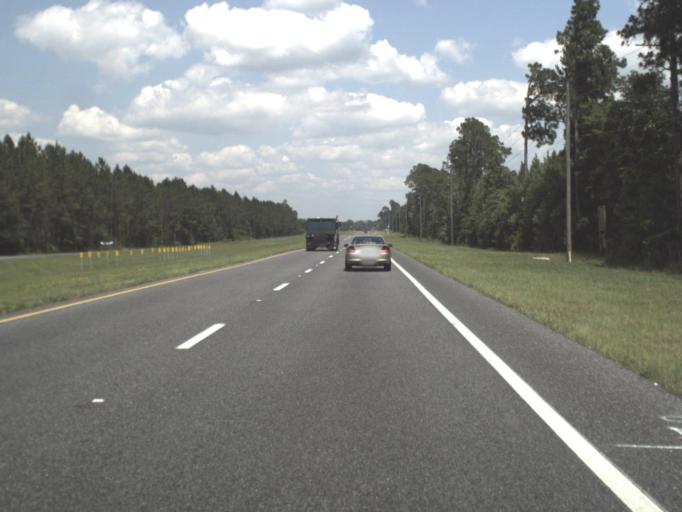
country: US
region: Florida
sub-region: Alachua County
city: Hawthorne
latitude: 29.5981
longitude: -82.1176
